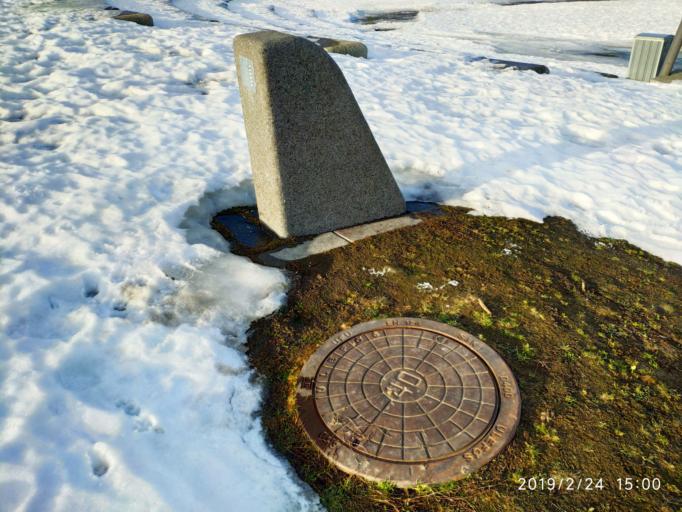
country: NO
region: Akershus
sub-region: Lorenskog
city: Kjenn
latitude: 59.9307
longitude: 10.9624
